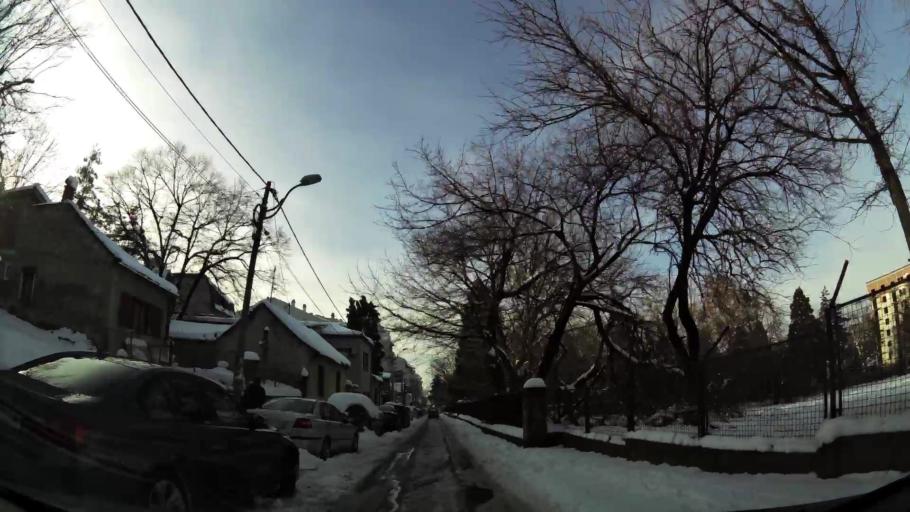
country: RS
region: Central Serbia
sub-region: Belgrade
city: Palilula
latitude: 44.7990
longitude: 20.4975
